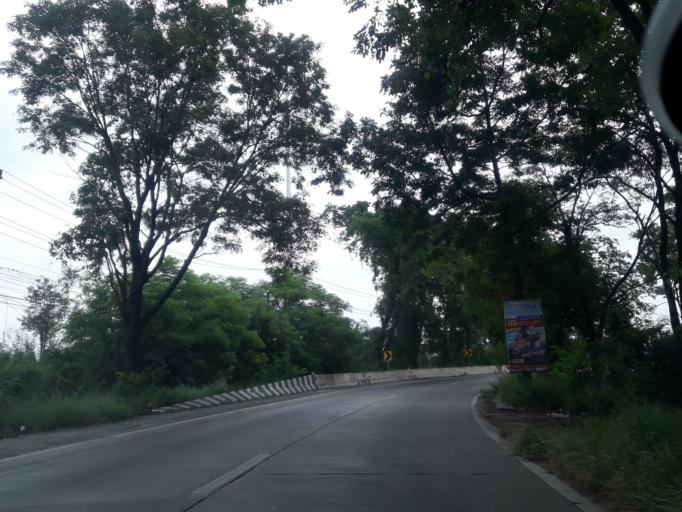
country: TH
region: Sara Buri
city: Kaeng Khoi
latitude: 14.5806
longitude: 101.0013
